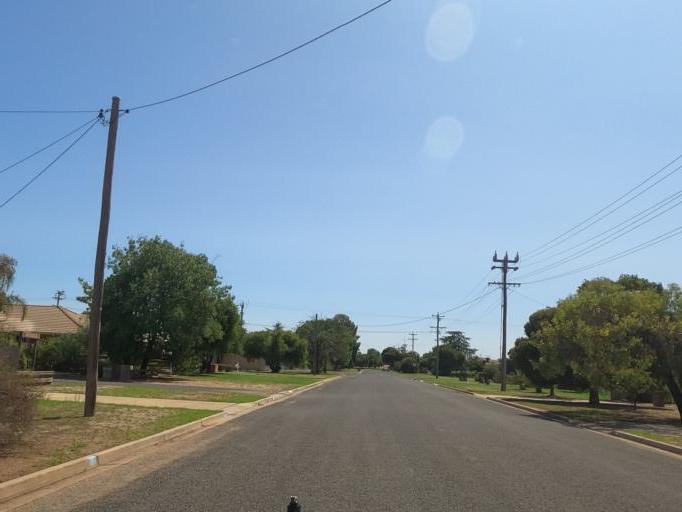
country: AU
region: New South Wales
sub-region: Corowa Shire
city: Mulwala
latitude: -35.9848
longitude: 146.0079
